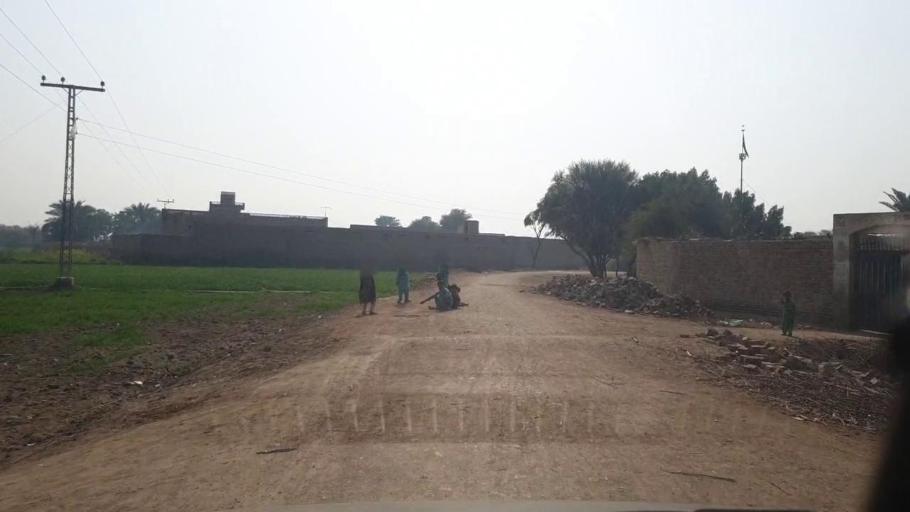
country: PK
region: Sindh
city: Shahdadpur
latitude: 26.0339
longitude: 68.5108
